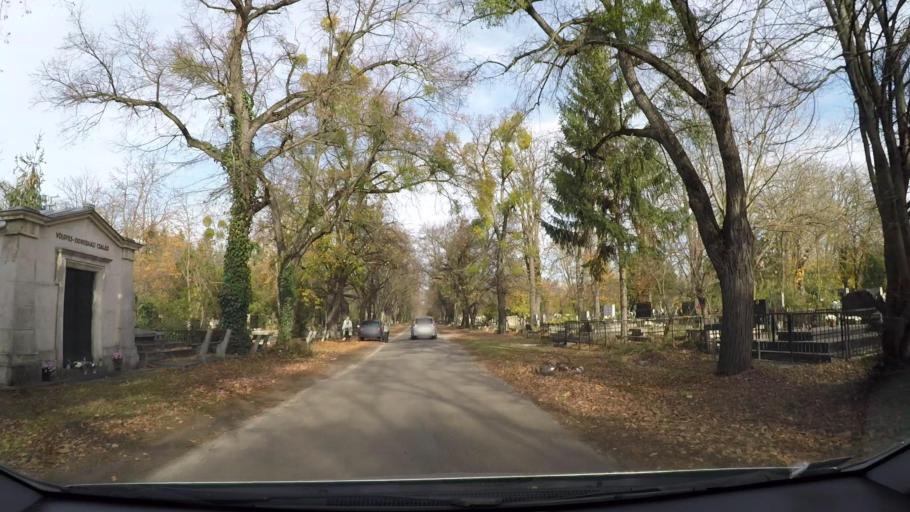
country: HU
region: Budapest
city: Budapest X. keruelet
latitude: 47.4735
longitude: 19.1847
